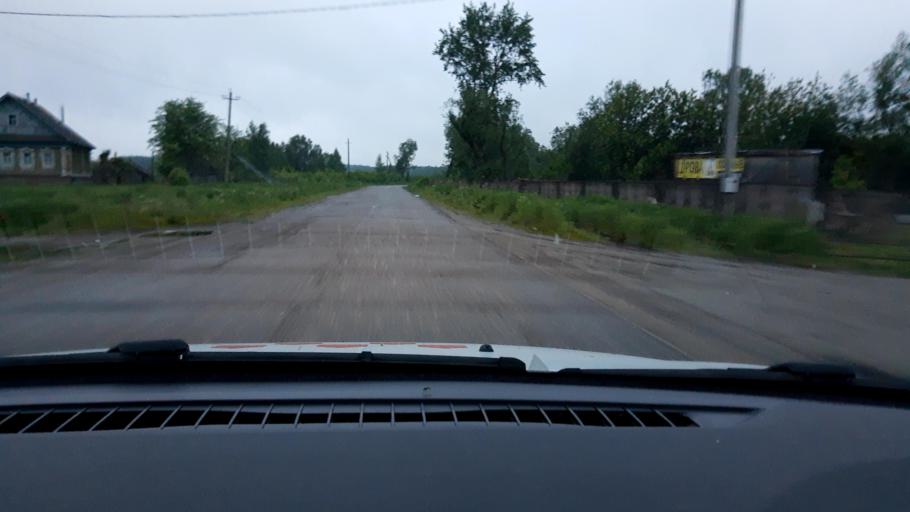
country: RU
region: Nizjnij Novgorod
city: Novaya Balakhna
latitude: 56.6322
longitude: 43.6167
